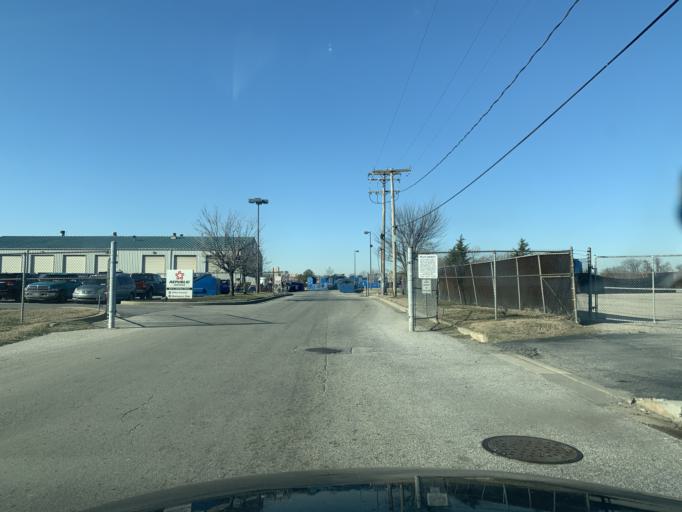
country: US
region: Maryland
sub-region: City of Baltimore
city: Baltimore
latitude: 39.2640
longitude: -76.6180
